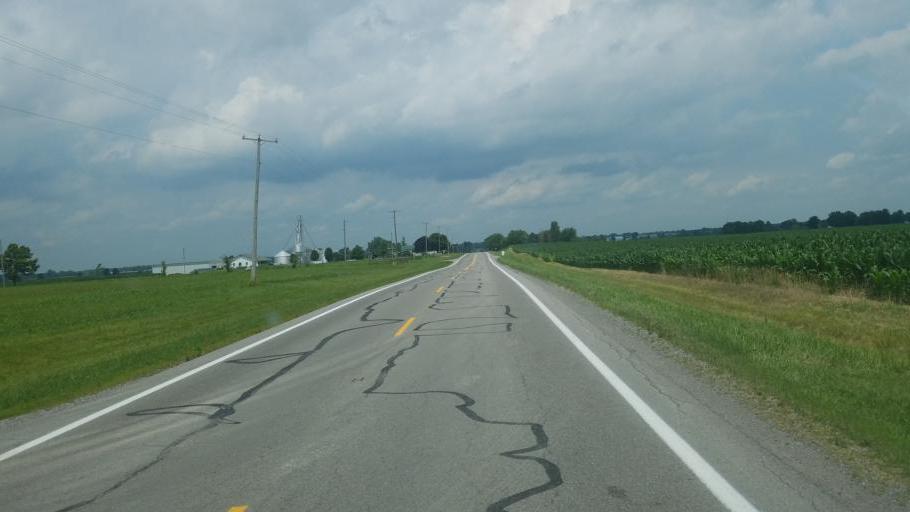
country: US
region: Ohio
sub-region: Hardin County
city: Kenton
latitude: 40.6102
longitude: -83.5956
